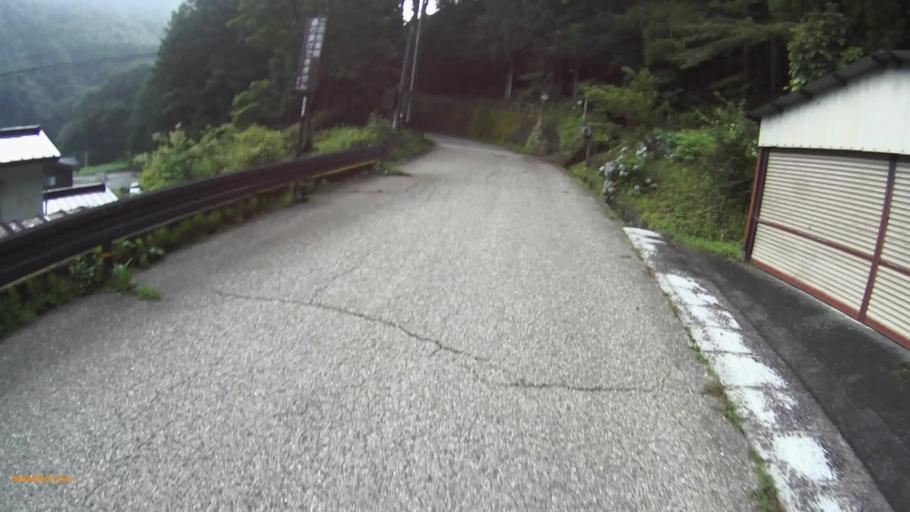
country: JP
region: Nagano
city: Tatsuno
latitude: 35.9611
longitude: 137.8081
